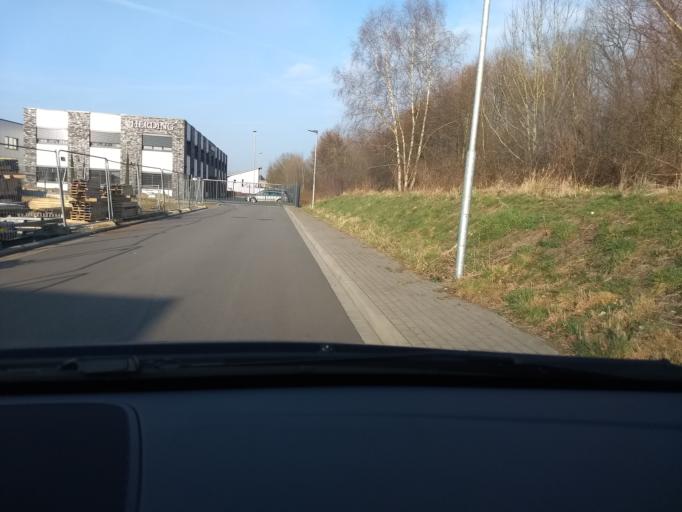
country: DE
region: North Rhine-Westphalia
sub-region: Regierungsbezirk Munster
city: Rhede
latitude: 51.8355
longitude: 6.7200
